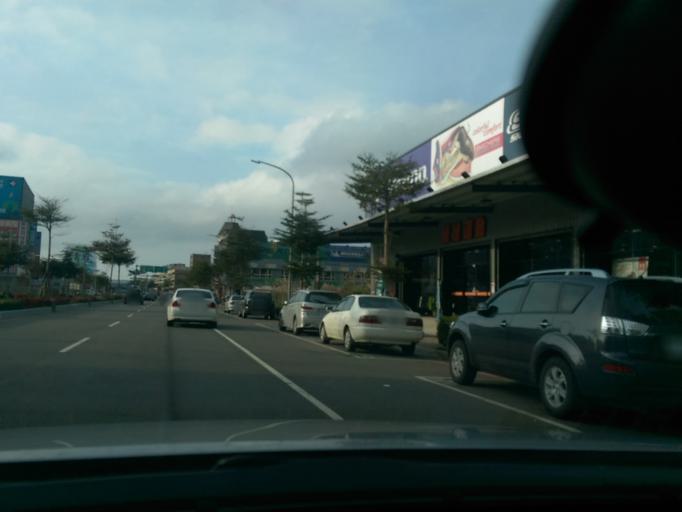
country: TW
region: Taiwan
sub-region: Taoyuan
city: Taoyuan
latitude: 25.0844
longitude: 121.3772
